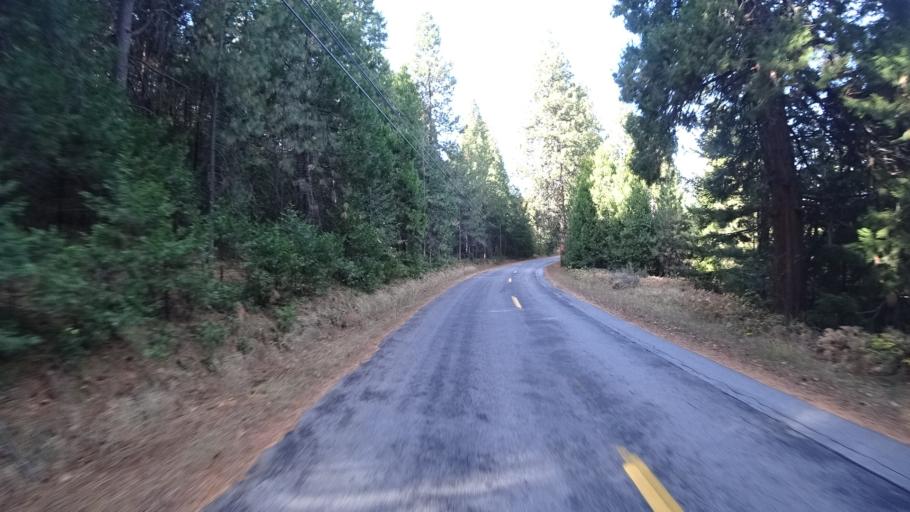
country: US
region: California
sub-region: Siskiyou County
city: Weed
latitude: 41.4306
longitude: -122.4055
